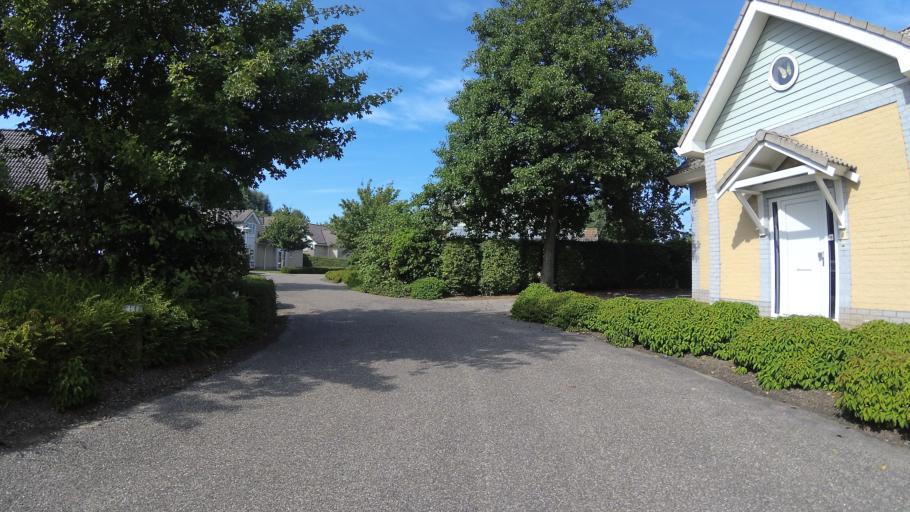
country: NL
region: Zeeland
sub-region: Gemeente Noord-Beveland
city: Kamperland
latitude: 51.5895
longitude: 3.6711
